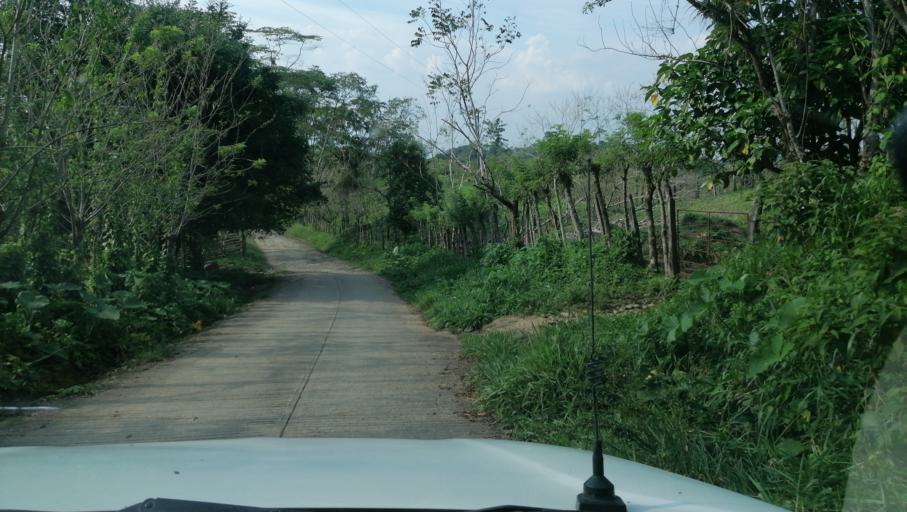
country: MX
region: Chiapas
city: Ostuacan
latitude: 17.4834
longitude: -93.2405
